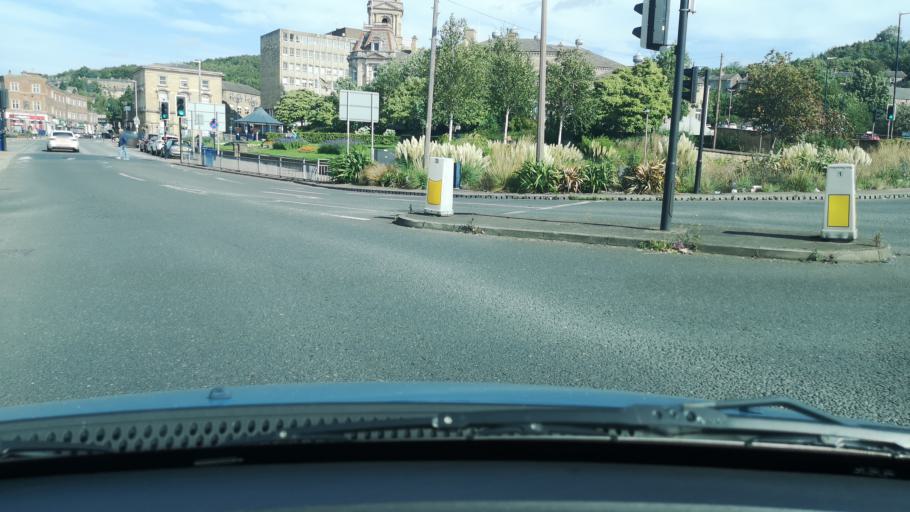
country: GB
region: England
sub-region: Kirklees
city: Dewsbury
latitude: 53.6904
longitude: -1.6278
